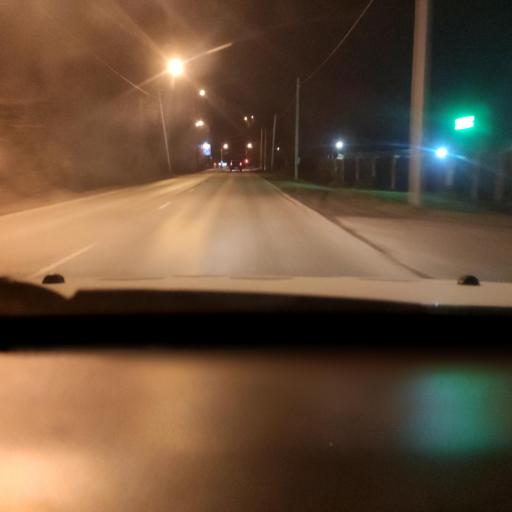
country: RU
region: Perm
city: Perm
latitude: 58.0592
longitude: 56.3377
